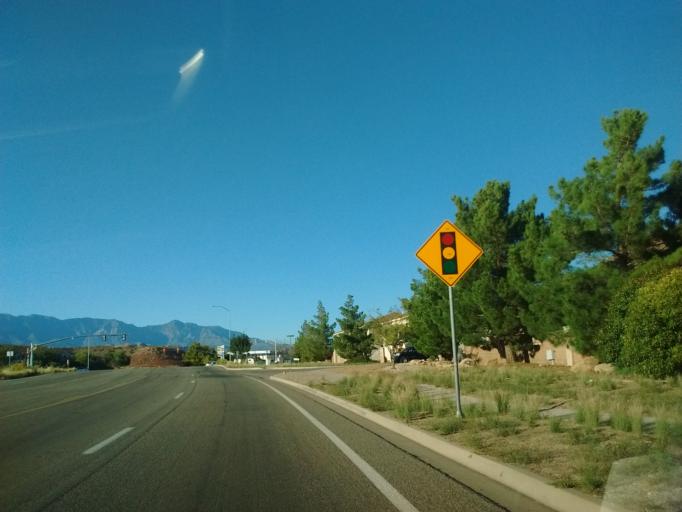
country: US
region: Utah
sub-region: Washington County
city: Washington
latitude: 37.1591
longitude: -113.4355
